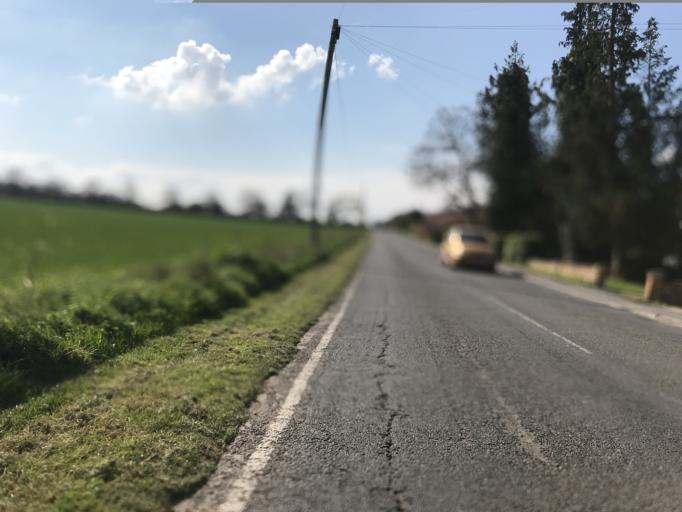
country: GB
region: England
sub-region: Cambridgeshire
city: Sawston
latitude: 52.1624
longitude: 0.1586
